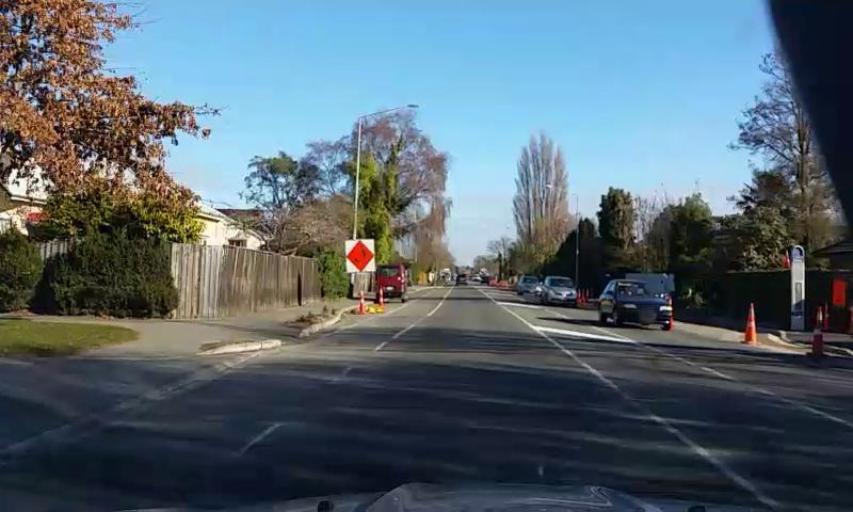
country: NZ
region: Canterbury
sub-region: Christchurch City
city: Christchurch
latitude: -43.5081
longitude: 172.6505
